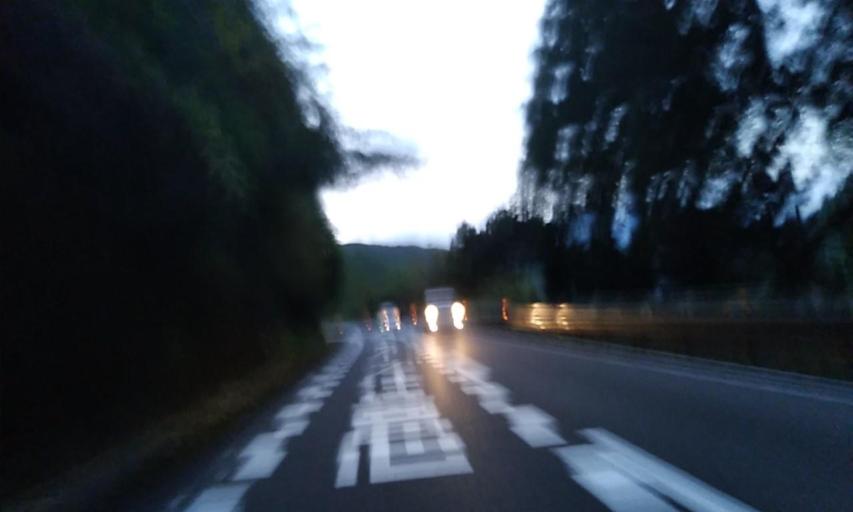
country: JP
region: Wakayama
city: Shingu
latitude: 33.7343
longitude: 135.9416
